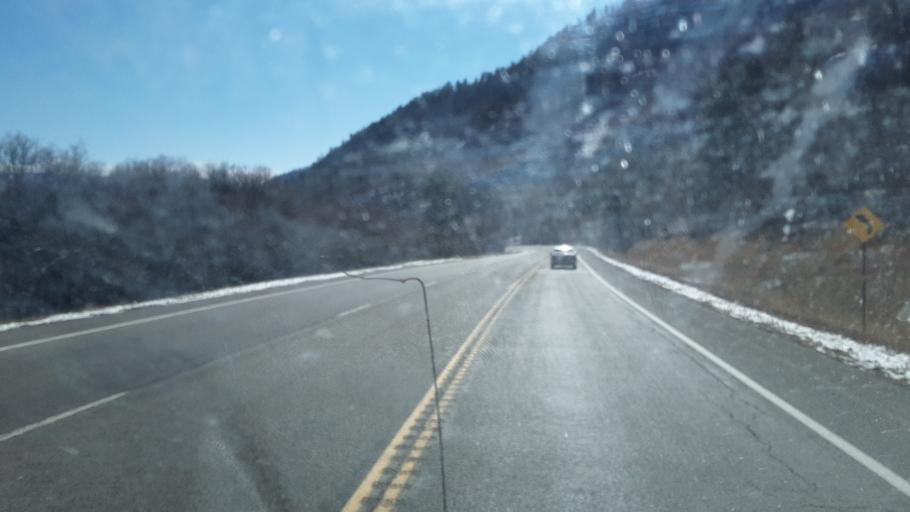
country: US
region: Colorado
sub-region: La Plata County
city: Durango
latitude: 37.5129
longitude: -107.8178
